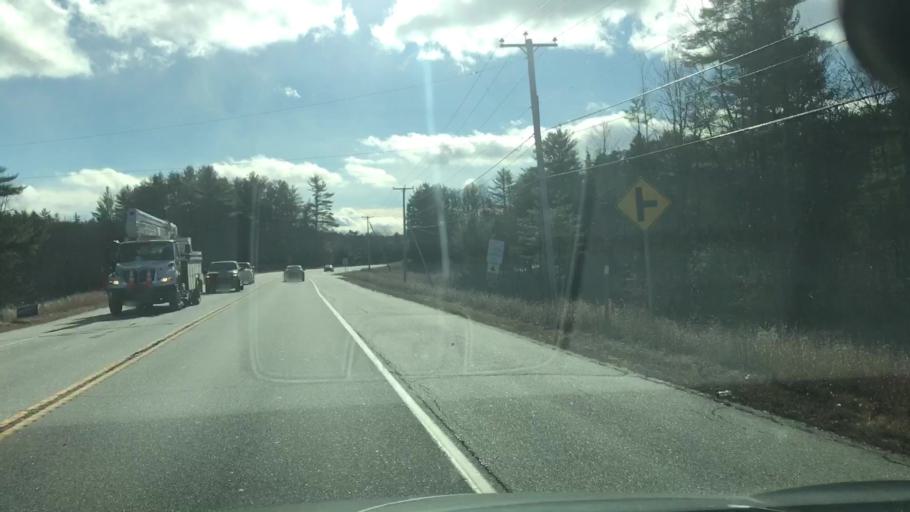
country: US
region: New Hampshire
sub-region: Belknap County
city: Barnstead
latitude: 43.3213
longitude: -71.3052
